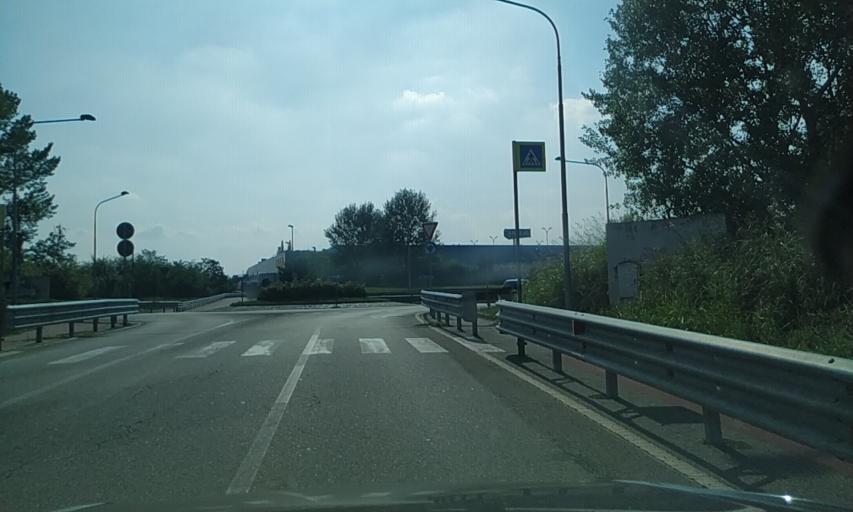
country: IT
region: Piedmont
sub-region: Provincia di Torino
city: Collegno
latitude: 45.0989
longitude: 7.5853
